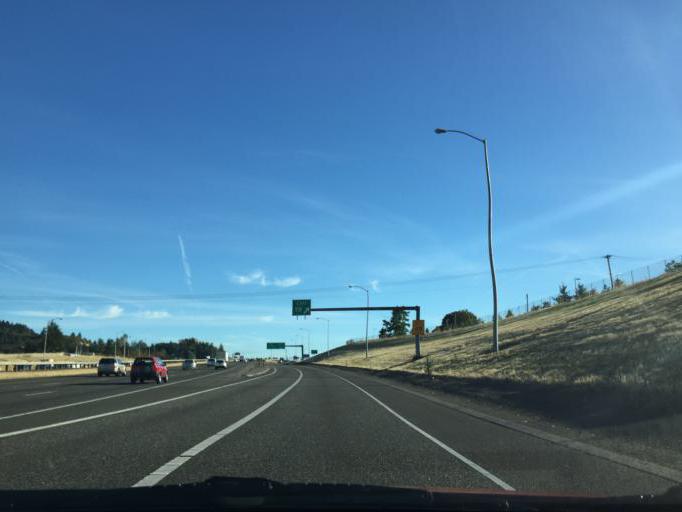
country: US
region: Oregon
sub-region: Multnomah County
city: Lents
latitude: 45.5099
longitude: -122.5657
